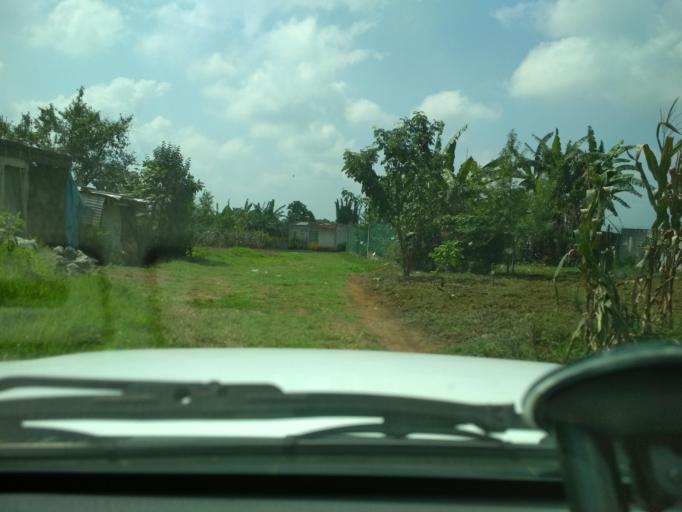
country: MX
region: Veracruz
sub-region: Fortin
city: Santa Lucia Potrerillo
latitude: 18.9667
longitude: -97.0265
